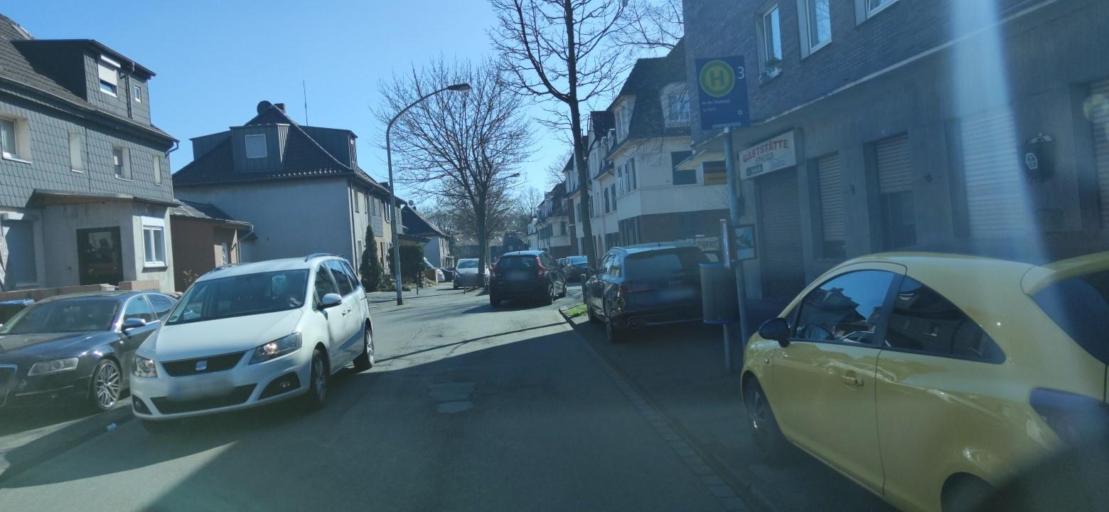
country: DE
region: North Rhine-Westphalia
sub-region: Regierungsbezirk Dusseldorf
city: Hochfeld
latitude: 51.3667
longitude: 6.7238
